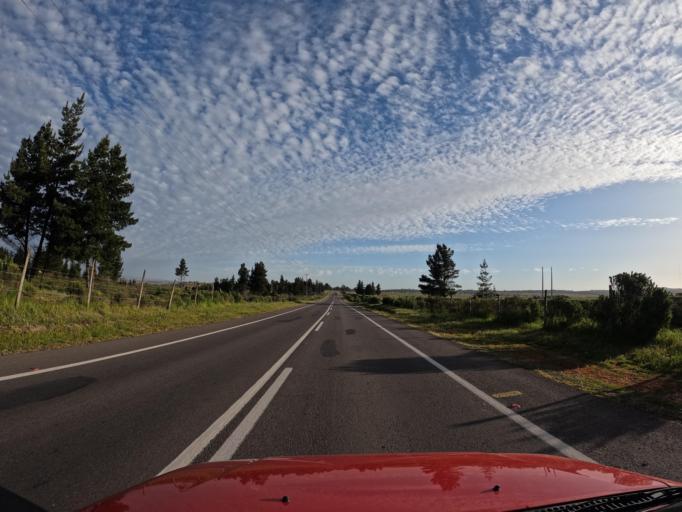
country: CL
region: Valparaiso
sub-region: San Antonio Province
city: San Antonio
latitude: -34.0572
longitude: -71.6257
